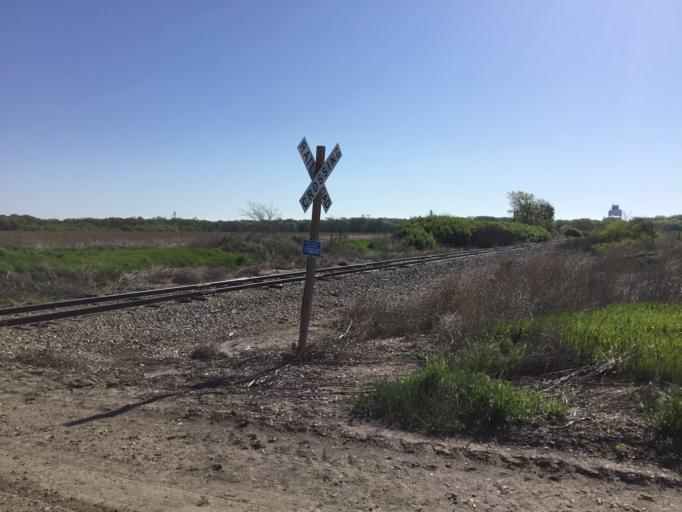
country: US
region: Kansas
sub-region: Smith County
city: Smith Center
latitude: 39.7635
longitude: -99.0479
